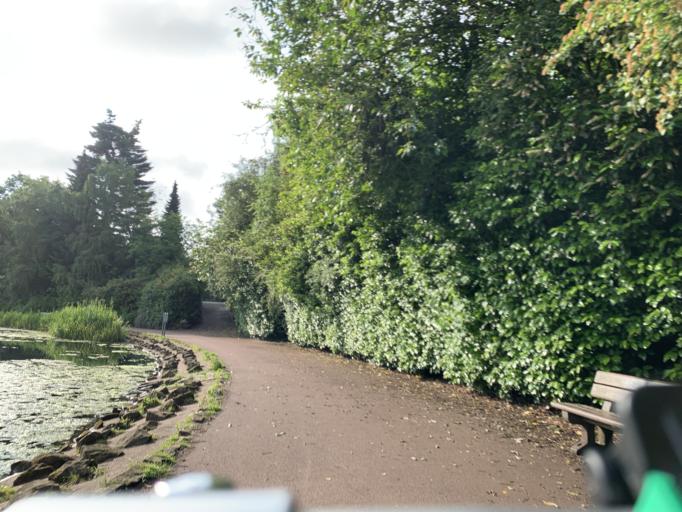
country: GB
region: Scotland
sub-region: East Renfrewshire
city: Giffnock
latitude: 55.7912
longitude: -4.3145
